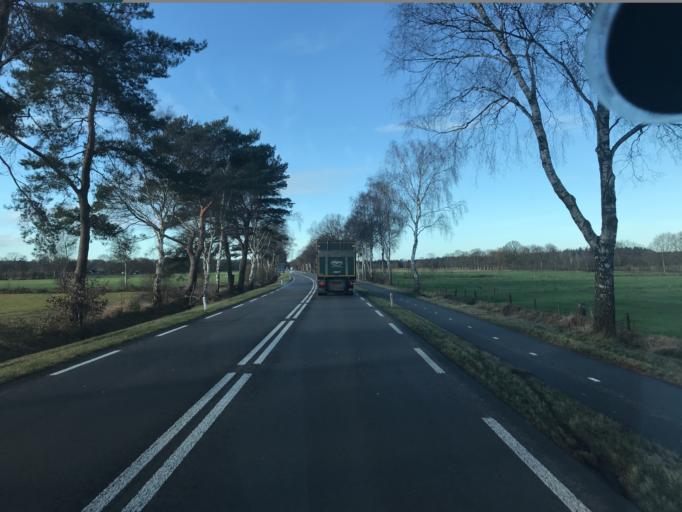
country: NL
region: Gelderland
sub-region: Gemeente Barneveld
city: Garderen
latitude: 52.2762
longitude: 5.7240
